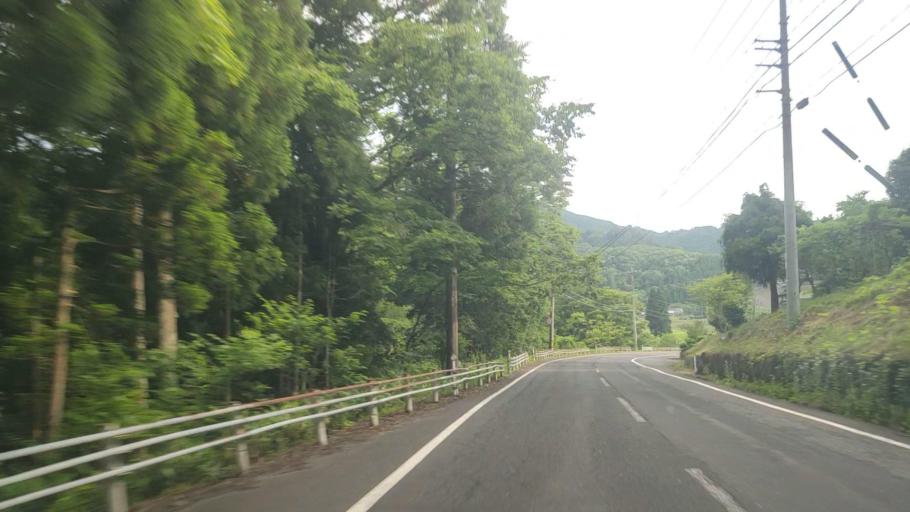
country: JP
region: Tottori
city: Kurayoshi
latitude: 35.2942
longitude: 133.9496
